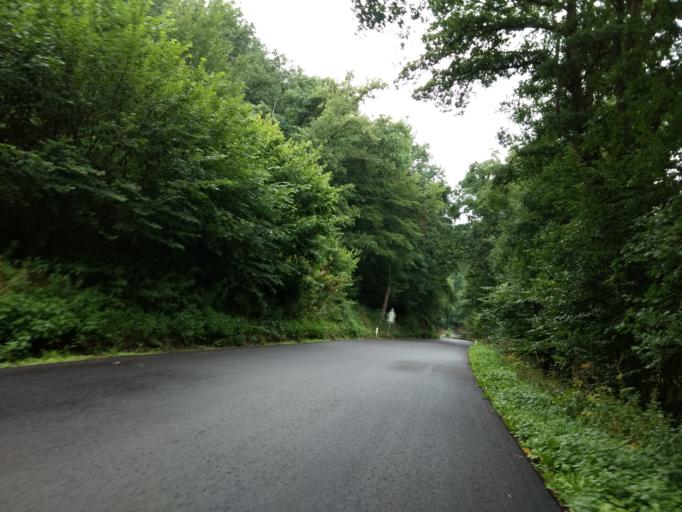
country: BE
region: Wallonia
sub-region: Province du Luxembourg
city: Houffalize
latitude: 50.1361
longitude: 5.7524
